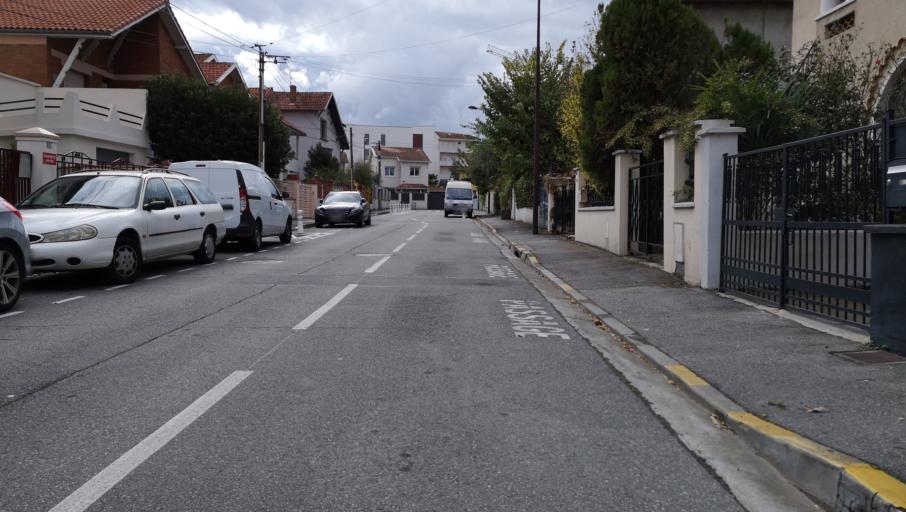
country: FR
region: Midi-Pyrenees
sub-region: Departement de la Haute-Garonne
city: Toulouse
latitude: 43.6037
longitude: 1.4109
